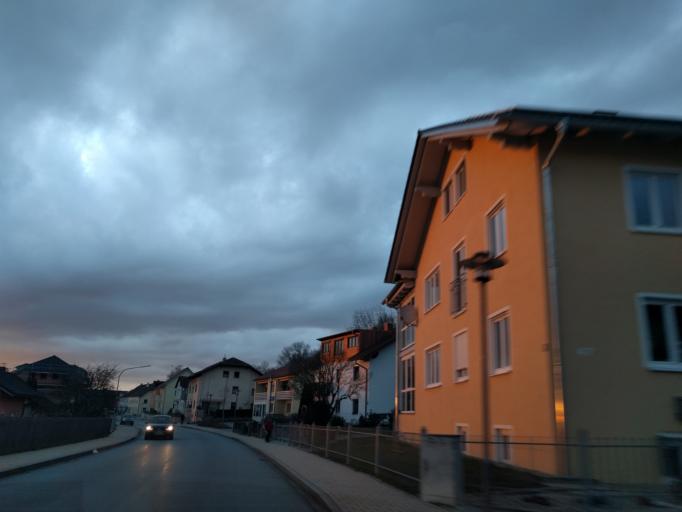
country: DE
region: Bavaria
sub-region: Lower Bavaria
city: Winzer
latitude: 48.7257
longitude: 13.0725
